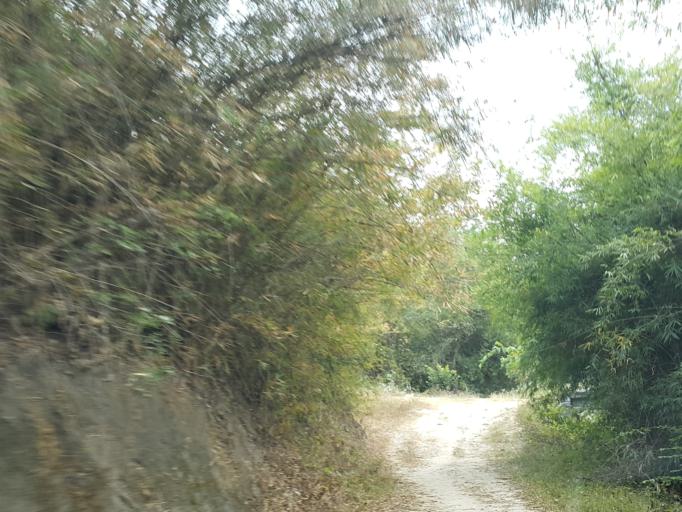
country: TH
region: Chiang Mai
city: Om Koi
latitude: 17.7976
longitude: 98.3364
